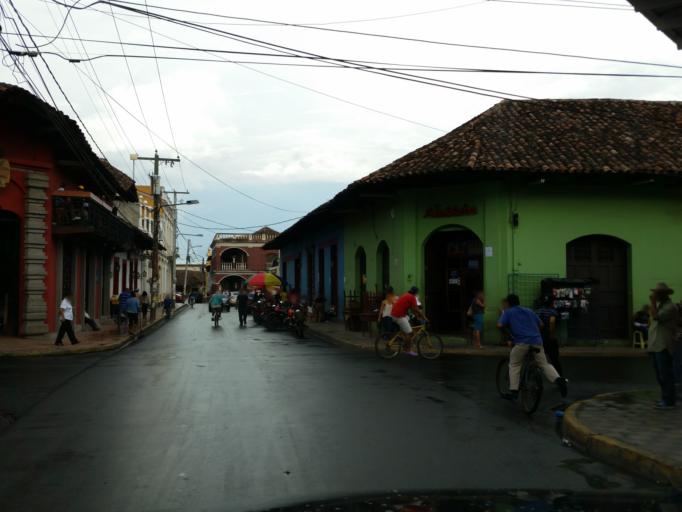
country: NI
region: Granada
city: Granada
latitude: 11.9293
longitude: -85.9553
